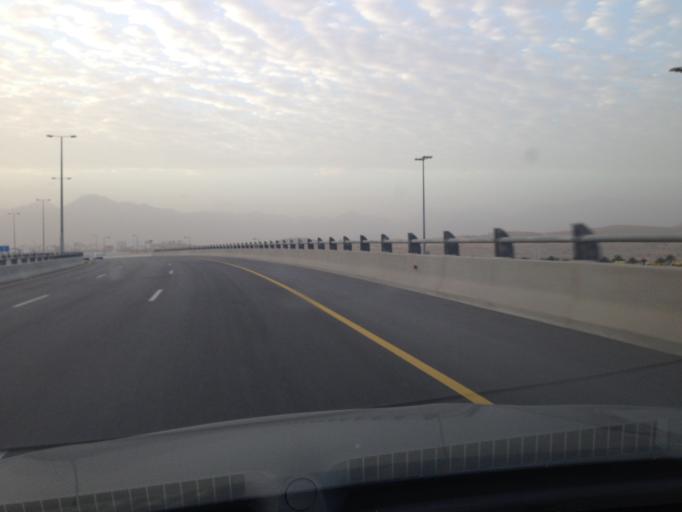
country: OM
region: Muhafazat Masqat
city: Bawshar
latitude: 23.5707
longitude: 58.3330
